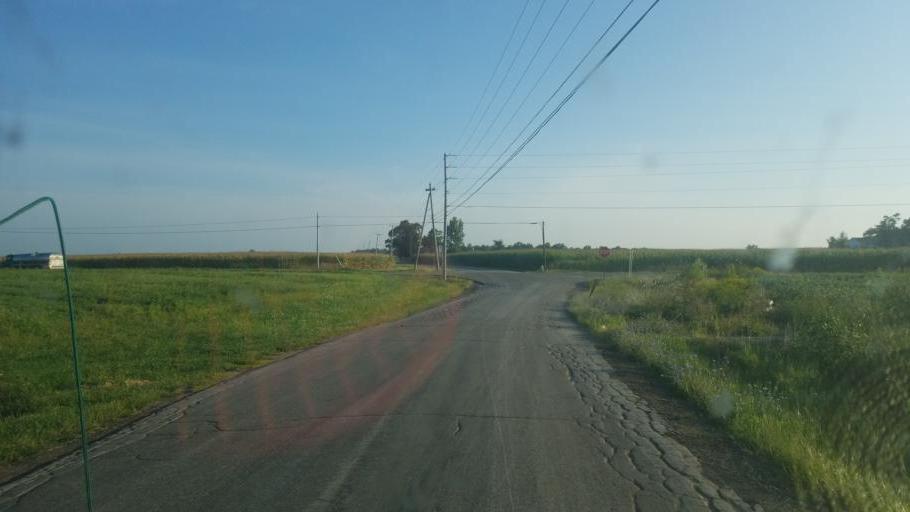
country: US
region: Ohio
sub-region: Richland County
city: Lincoln Heights
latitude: 40.9023
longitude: -82.4745
